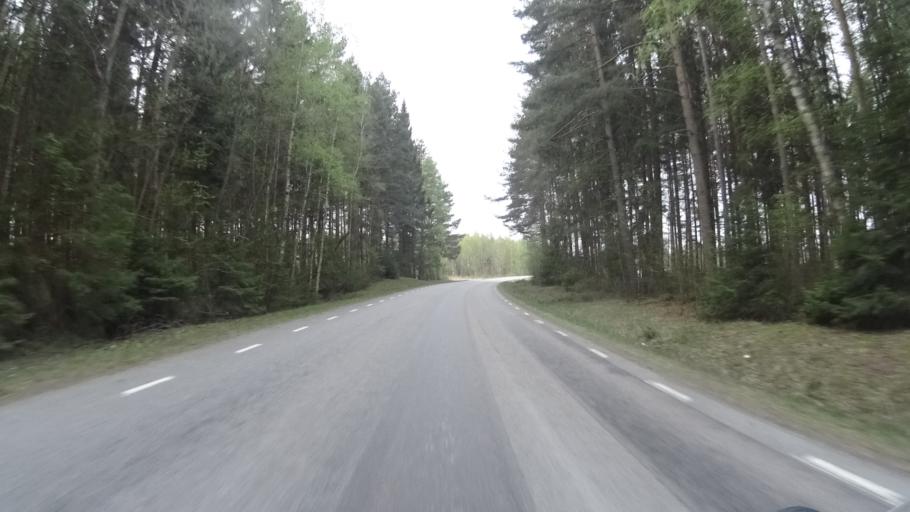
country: SE
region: Vaestra Goetaland
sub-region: Lidkopings Kommun
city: Vinninga
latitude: 58.4247
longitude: 13.3502
